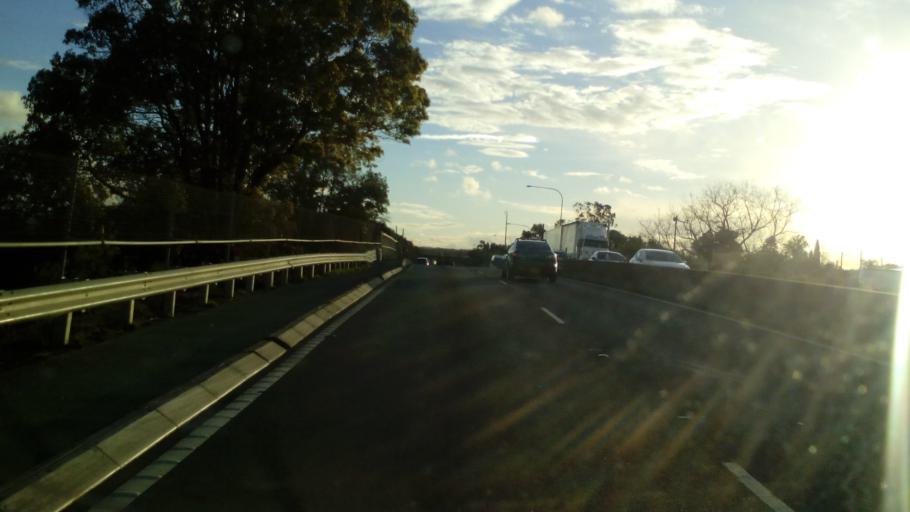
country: AU
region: New South Wales
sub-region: Newcastle
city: Beresfield
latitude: -32.8105
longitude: 151.6721
